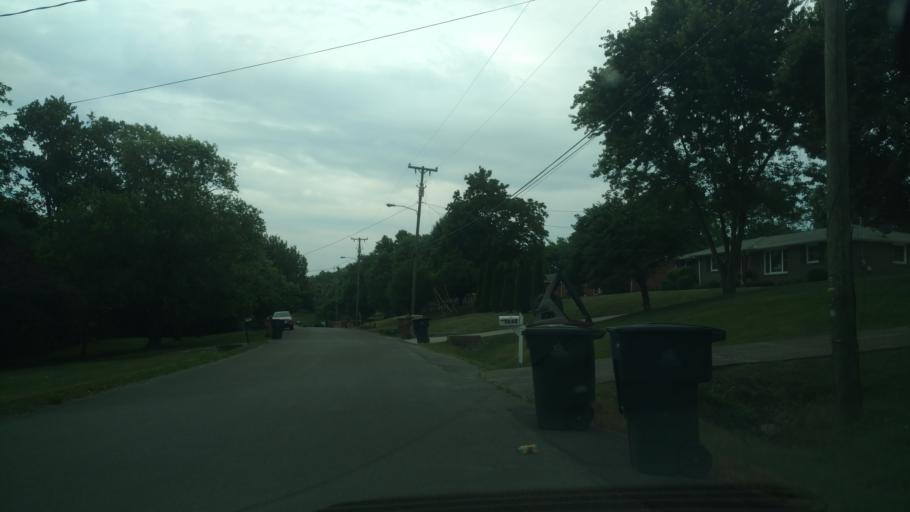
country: US
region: Tennessee
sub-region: Davidson County
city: Nashville
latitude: 36.2011
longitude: -86.7091
